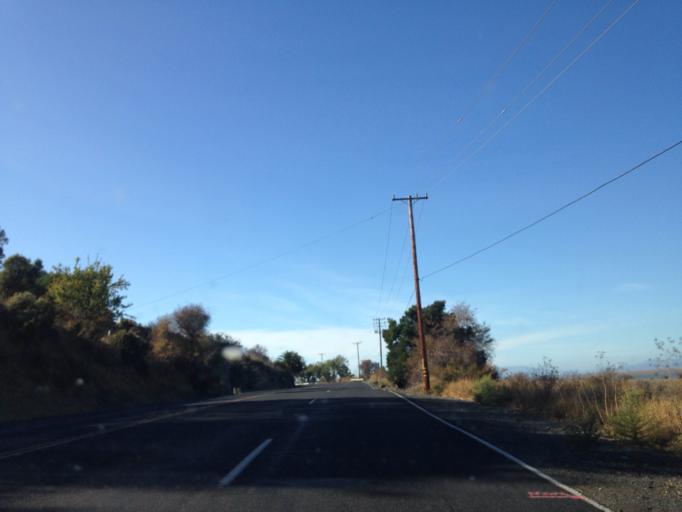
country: US
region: California
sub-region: Contra Costa County
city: Rodeo
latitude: 38.0482
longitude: -122.2506
